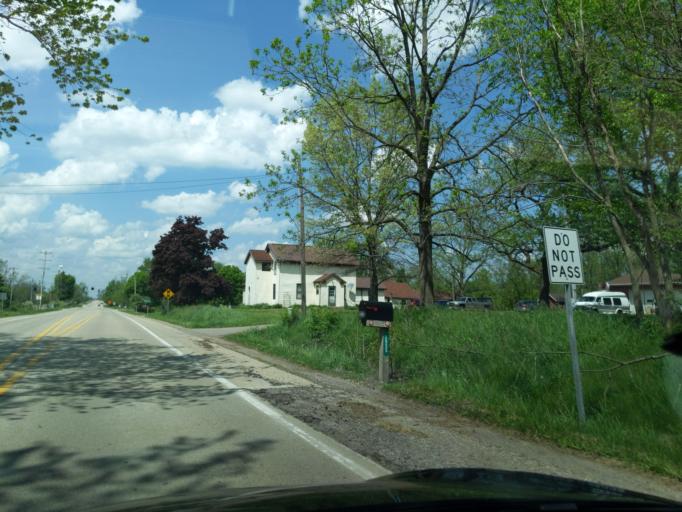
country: US
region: Michigan
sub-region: Ingham County
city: Okemos
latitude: 42.6677
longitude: -84.4329
